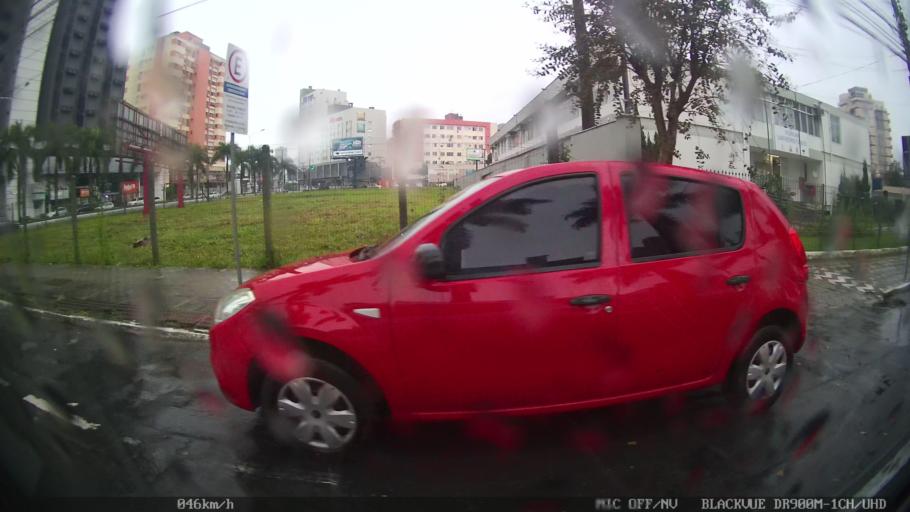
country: BR
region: Santa Catarina
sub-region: Itajai
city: Itajai
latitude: -26.9125
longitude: -48.6597
